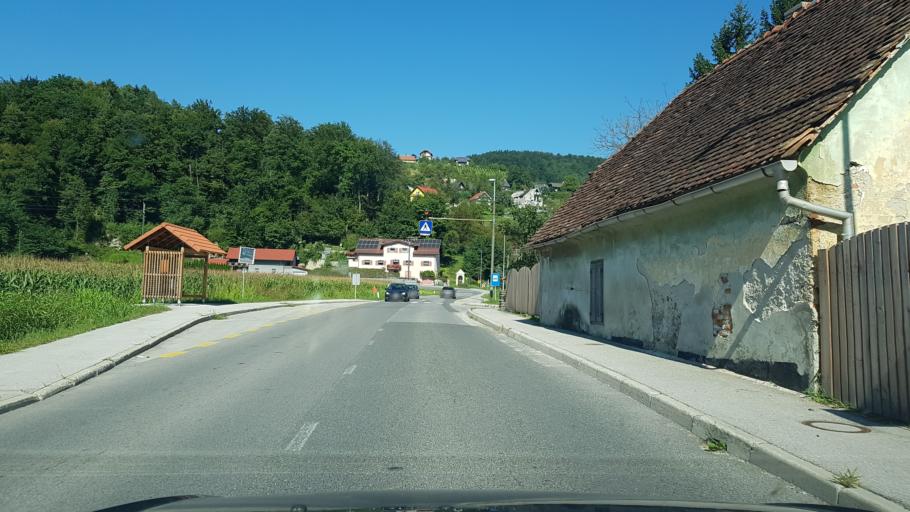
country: SI
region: Smartno ob Paki
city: Smartno ob Paki
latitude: 46.3315
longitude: 15.0331
